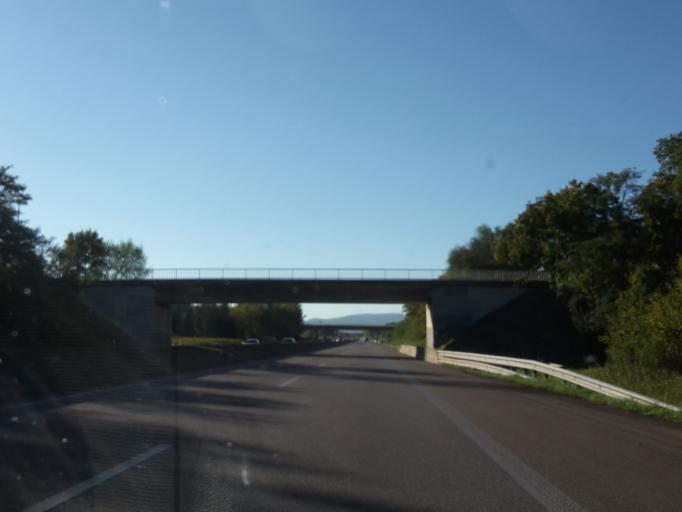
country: DE
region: Rheinland-Pfalz
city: Birkenheide
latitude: 49.4726
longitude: 8.2609
